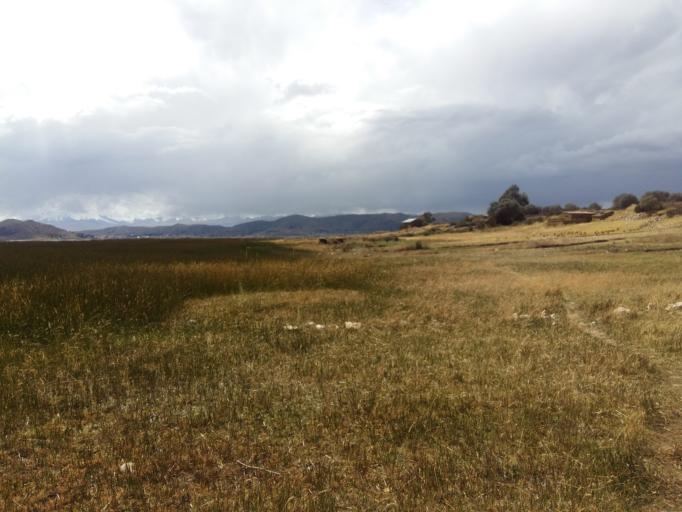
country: BO
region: La Paz
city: Batallas
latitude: -16.2825
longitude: -68.5977
